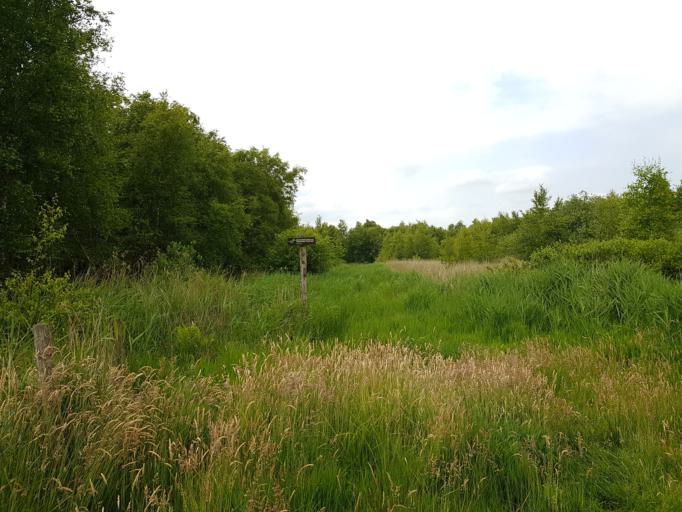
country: NL
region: Friesland
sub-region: Gemeente Tytsjerksteradiel
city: Garyp
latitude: 53.1385
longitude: 5.9472
